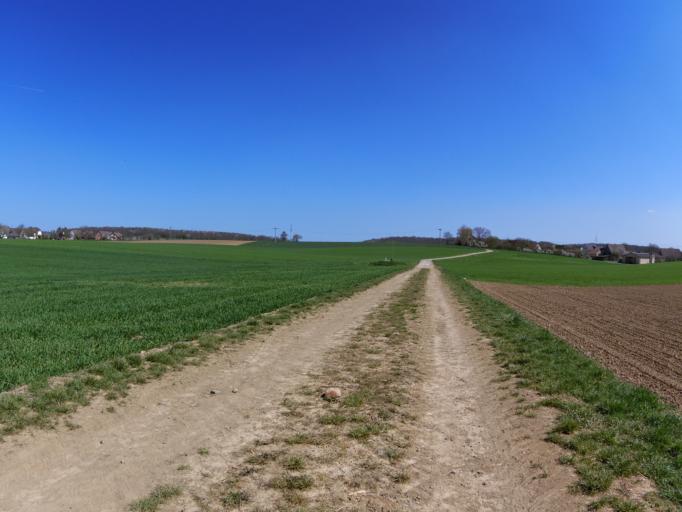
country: DE
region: Bavaria
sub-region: Regierungsbezirk Unterfranken
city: Rottendorf
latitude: 49.8139
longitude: 10.0483
